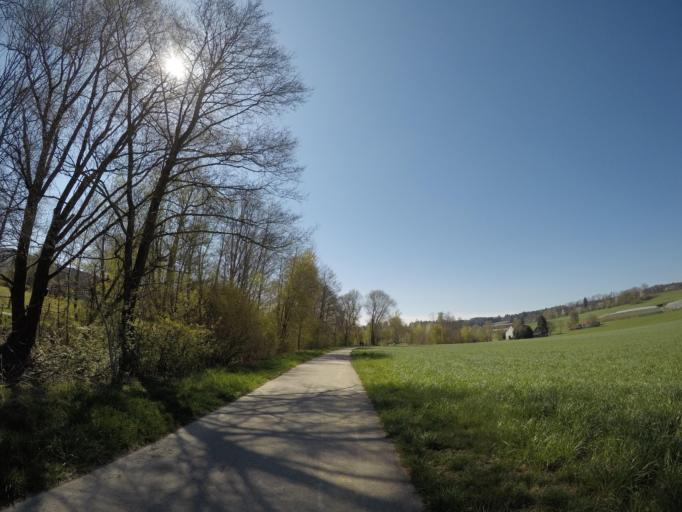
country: DE
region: Baden-Wuerttemberg
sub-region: Tuebingen Region
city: Horgenzell
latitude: 47.8264
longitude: 9.4584
